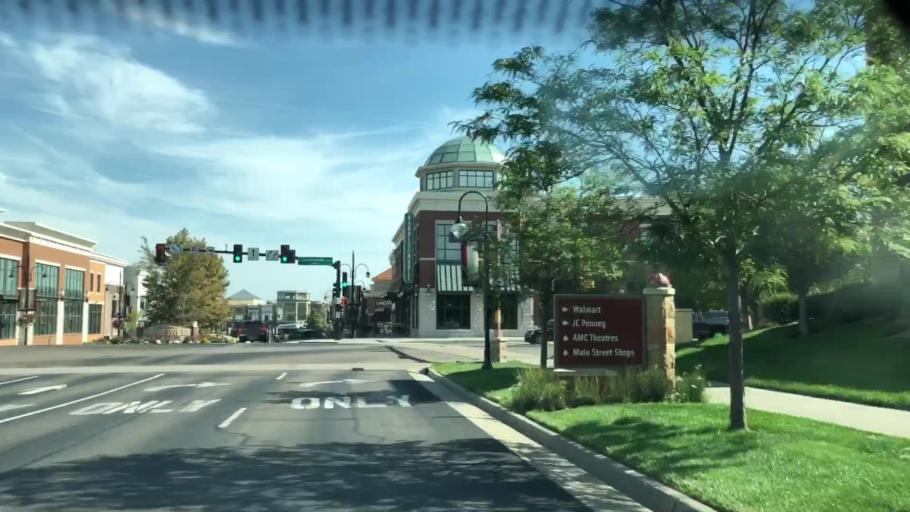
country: US
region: Colorado
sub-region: Douglas County
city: Parker
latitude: 39.6011
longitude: -104.7103
